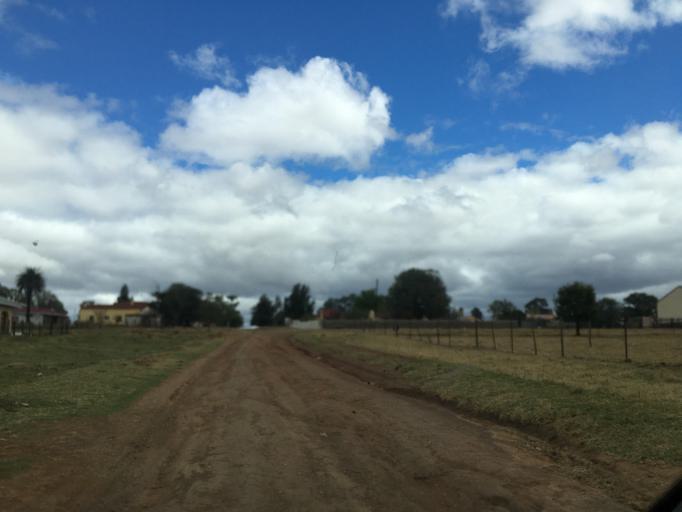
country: ZA
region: Eastern Cape
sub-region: Chris Hani District Municipality
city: Cala
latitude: -31.5226
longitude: 27.7025
